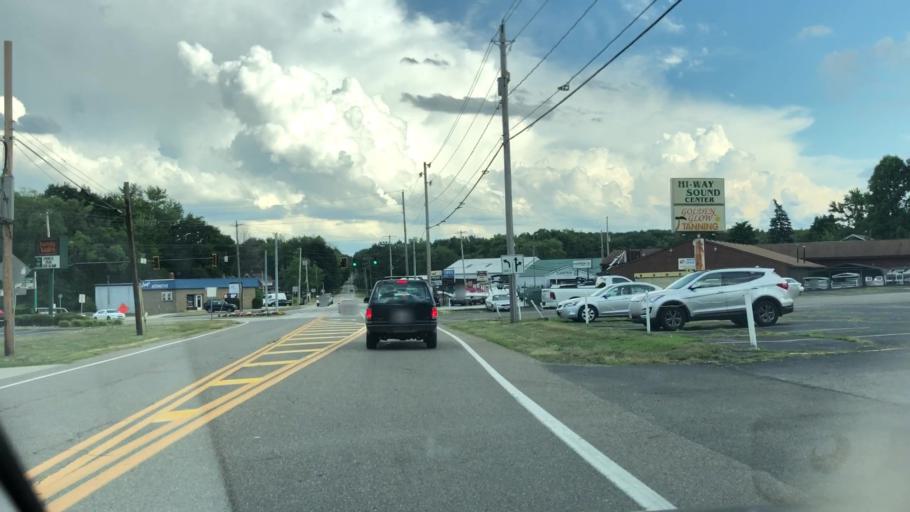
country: US
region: Ohio
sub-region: Summit County
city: Portage Lakes
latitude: 40.9985
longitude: -81.5580
